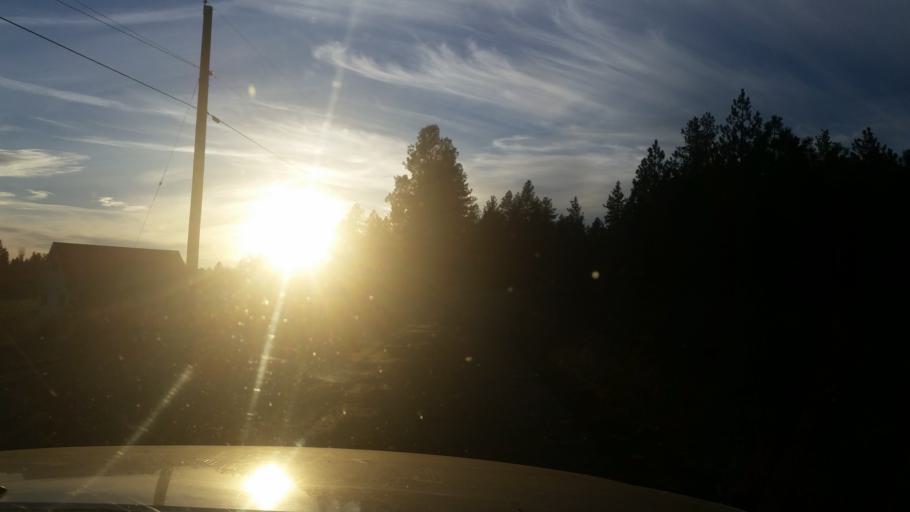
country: US
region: Washington
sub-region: Spokane County
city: Cheney
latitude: 47.5053
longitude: -117.5382
